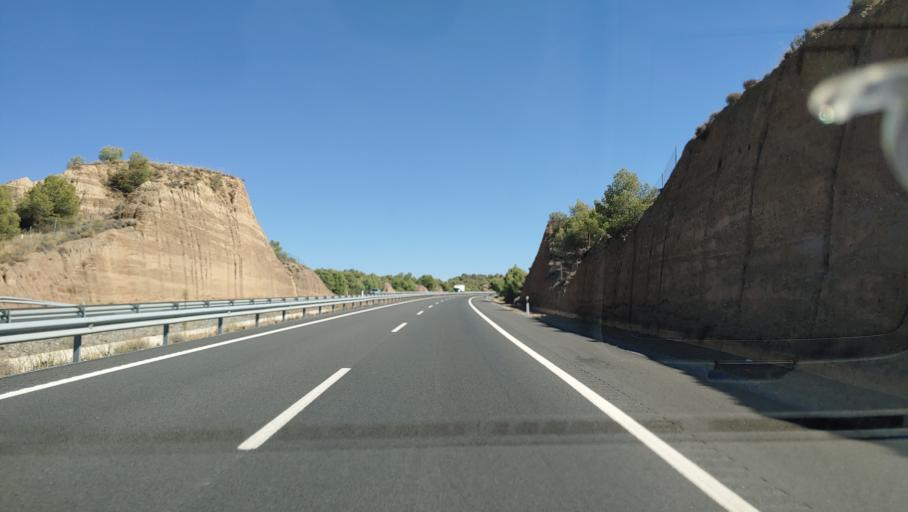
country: ES
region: Andalusia
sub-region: Provincia de Granada
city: Guadix
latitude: 37.2852
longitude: -3.1034
